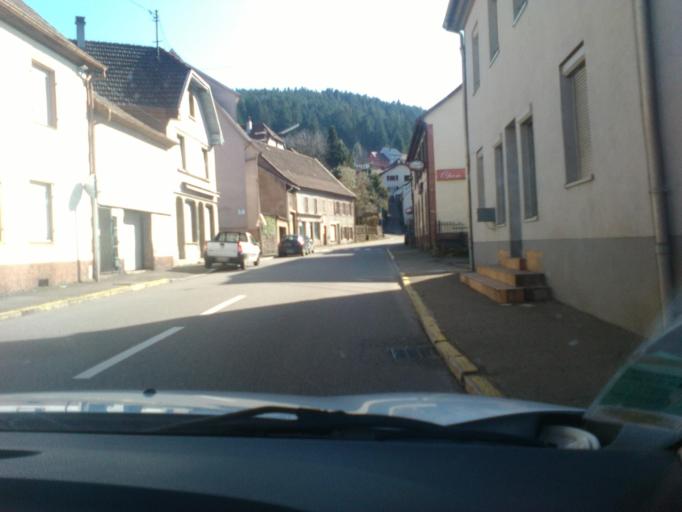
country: FR
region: Alsace
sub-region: Departement du Bas-Rhin
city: Rothau
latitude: 48.4564
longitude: 7.2071
